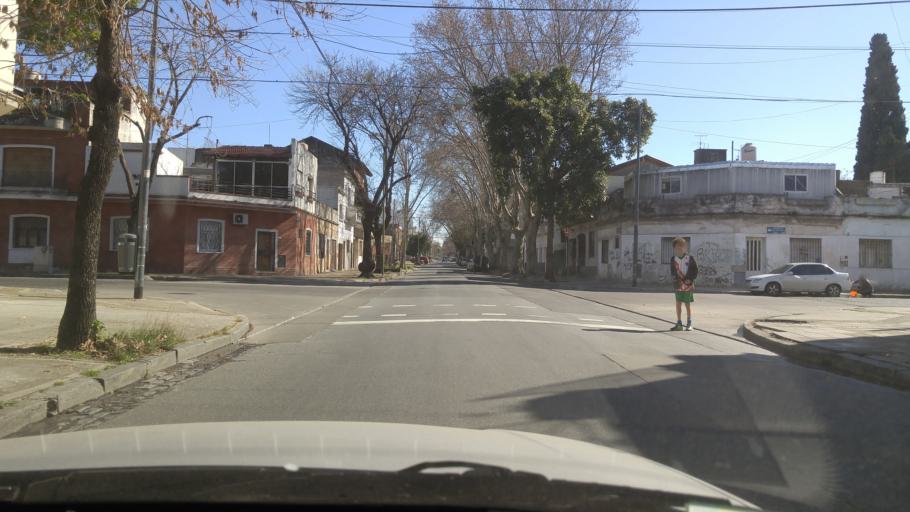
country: AR
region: Buenos Aires F.D.
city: Villa Santa Rita
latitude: -34.6235
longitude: -58.4898
